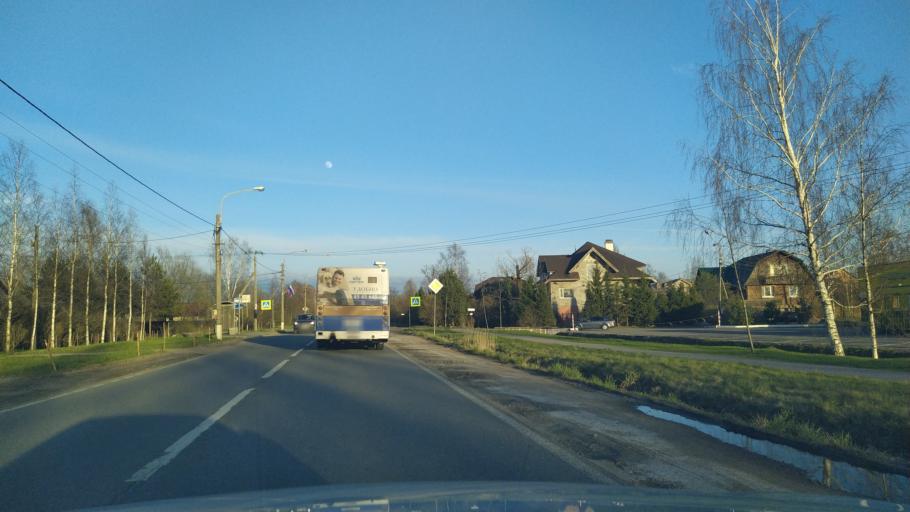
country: RU
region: St.-Petersburg
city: Aleksandrovskaya
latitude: 59.7365
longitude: 30.3322
